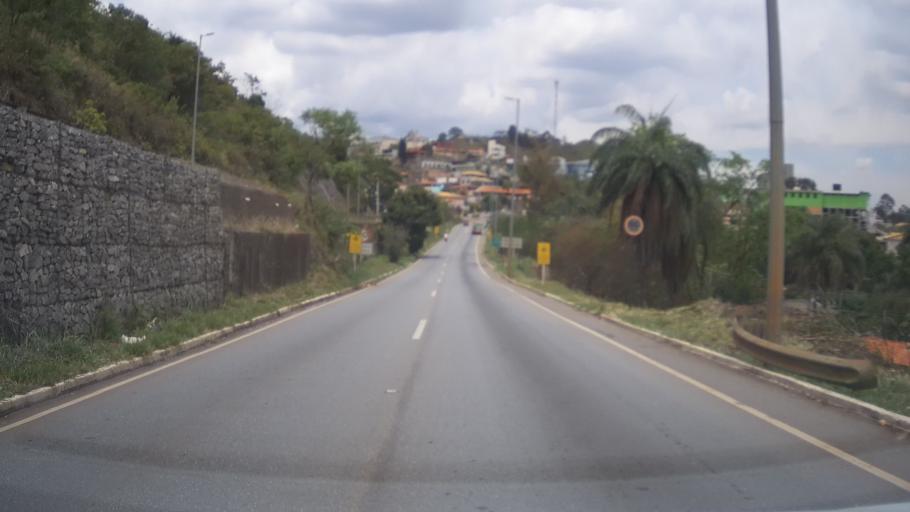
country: BR
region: Minas Gerais
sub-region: Nova Lima
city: Nova Lima
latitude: -19.9987
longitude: -43.8852
